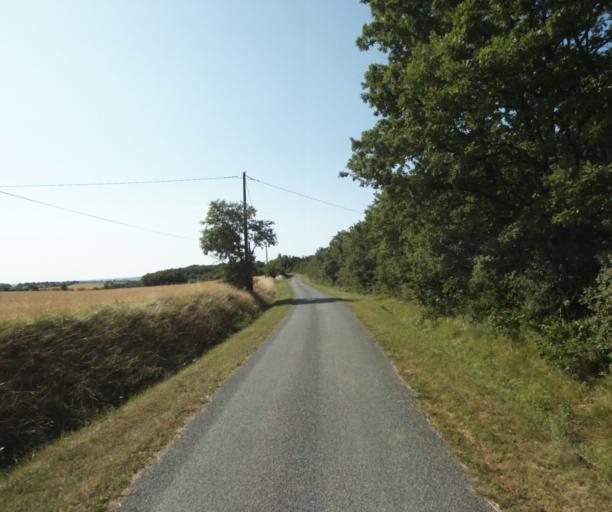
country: FR
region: Midi-Pyrenees
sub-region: Departement de la Haute-Garonne
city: Saint-Felix-Lauragais
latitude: 43.4260
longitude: 1.8412
